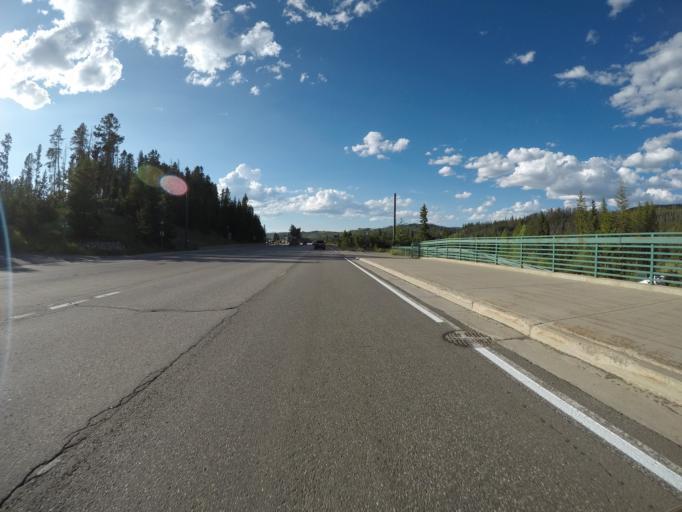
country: US
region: Colorado
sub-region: Grand County
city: Fraser
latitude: 39.9137
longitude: -105.7822
